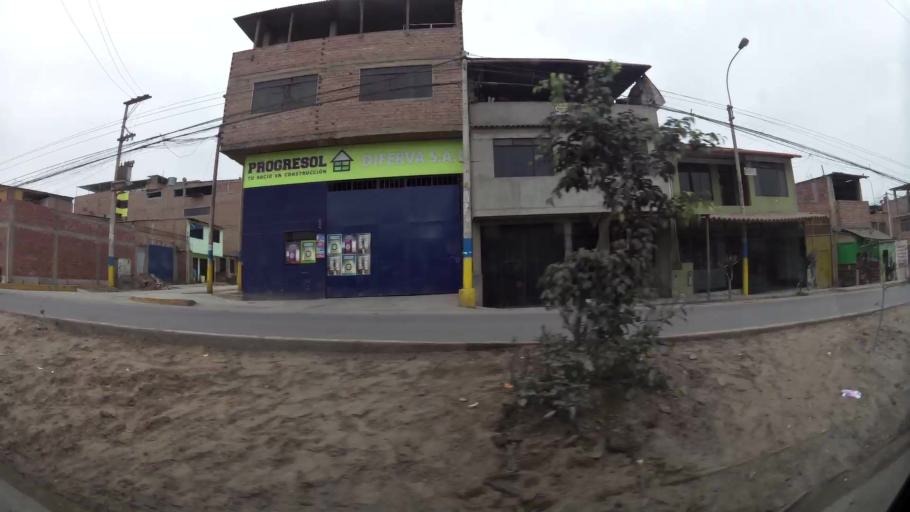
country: PE
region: Lima
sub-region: Lima
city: Surco
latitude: -12.2183
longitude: -76.9305
